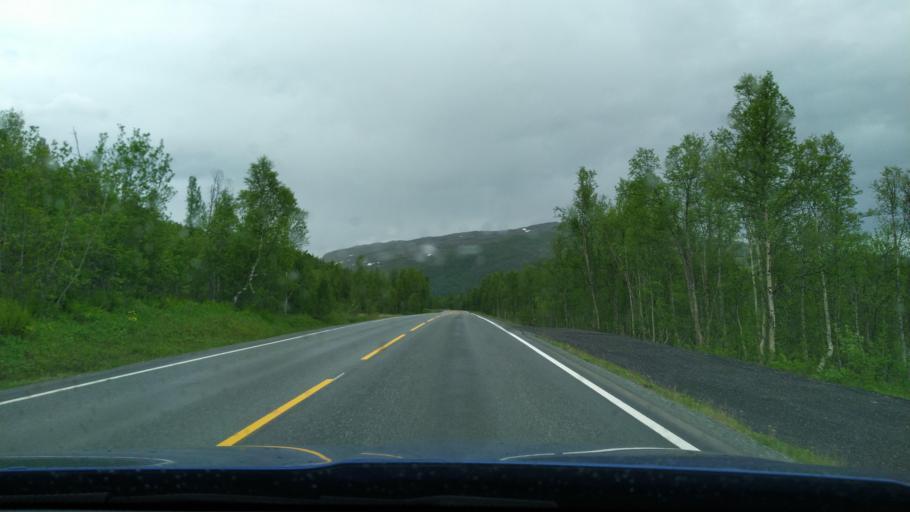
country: NO
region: Troms
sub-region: Balsfjord
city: Storsteinnes
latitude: 69.1323
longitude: 19.0147
